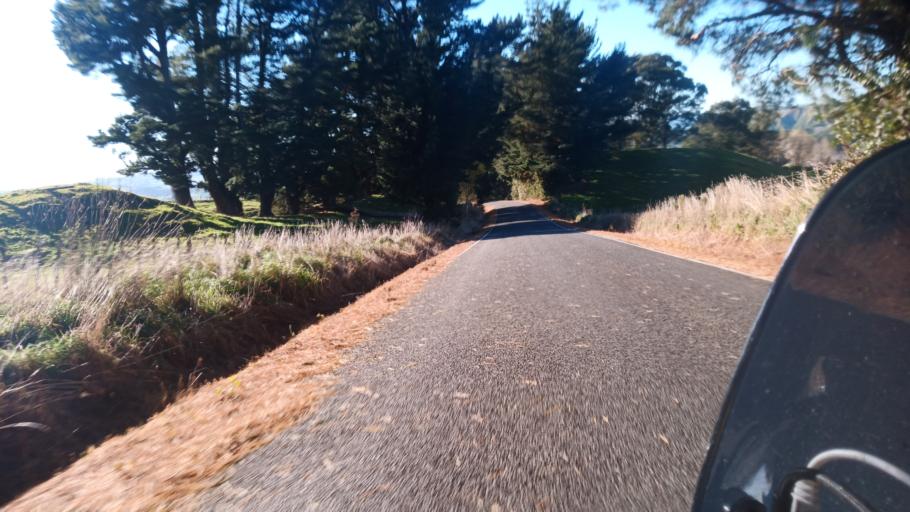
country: NZ
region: Hawke's Bay
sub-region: Wairoa District
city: Wairoa
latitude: -38.8329
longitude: 177.2696
